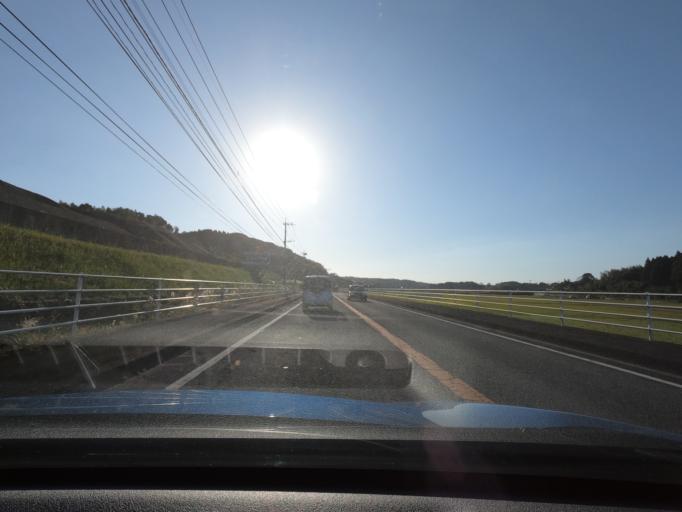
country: JP
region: Kagoshima
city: Akune
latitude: 32.0652
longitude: 130.2334
